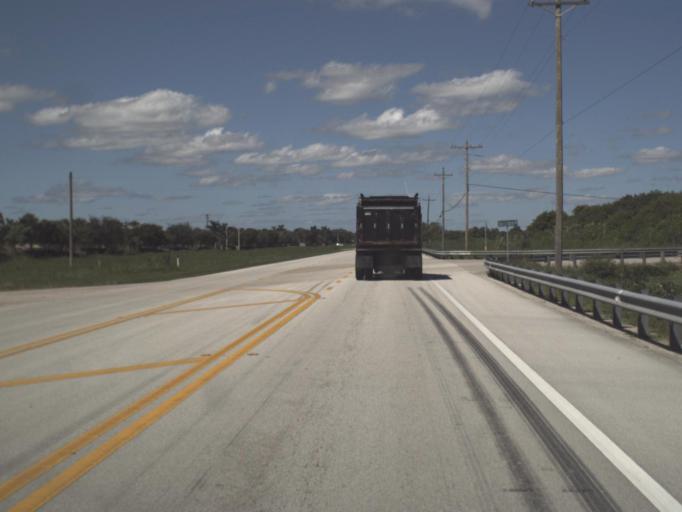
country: US
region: Florida
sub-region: Collier County
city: Lely Resort
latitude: 26.0137
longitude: -81.6217
